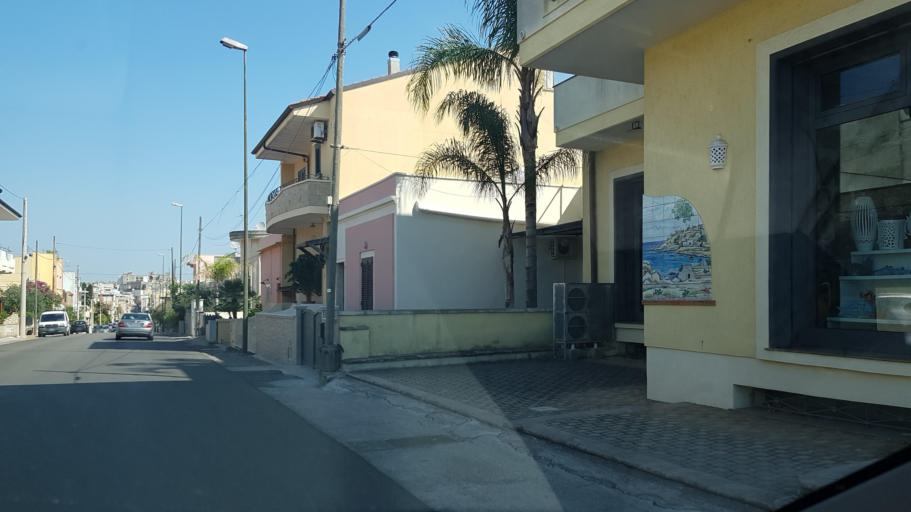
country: IT
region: Apulia
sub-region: Provincia di Lecce
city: Ruffano
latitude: 39.9774
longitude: 18.2528
